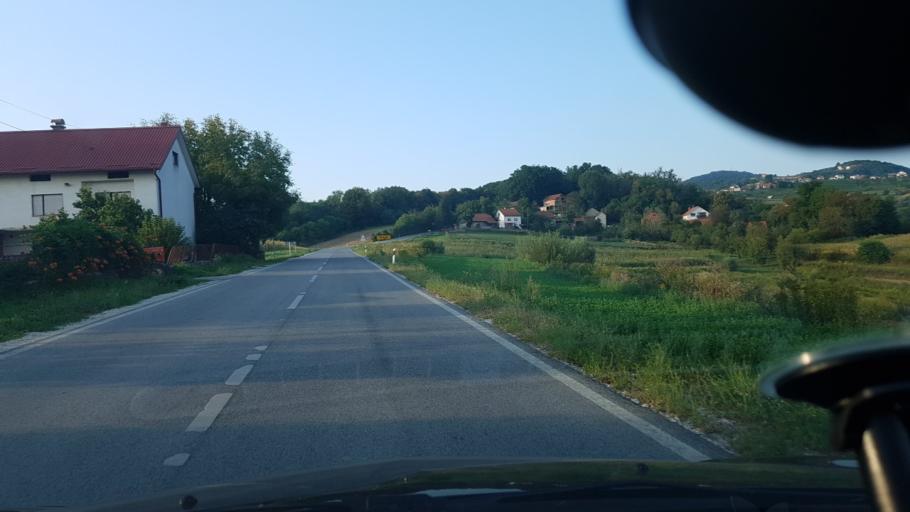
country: HR
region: Krapinsko-Zagorska
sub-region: Grad Krapina
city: Krapina
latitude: 46.1584
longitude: 15.8153
